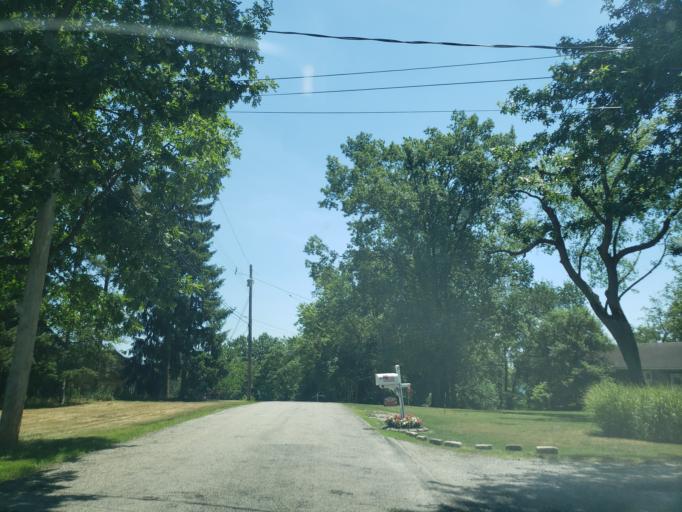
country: US
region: Pennsylvania
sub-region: Allegheny County
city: Emsworth
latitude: 40.5191
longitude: -80.0992
